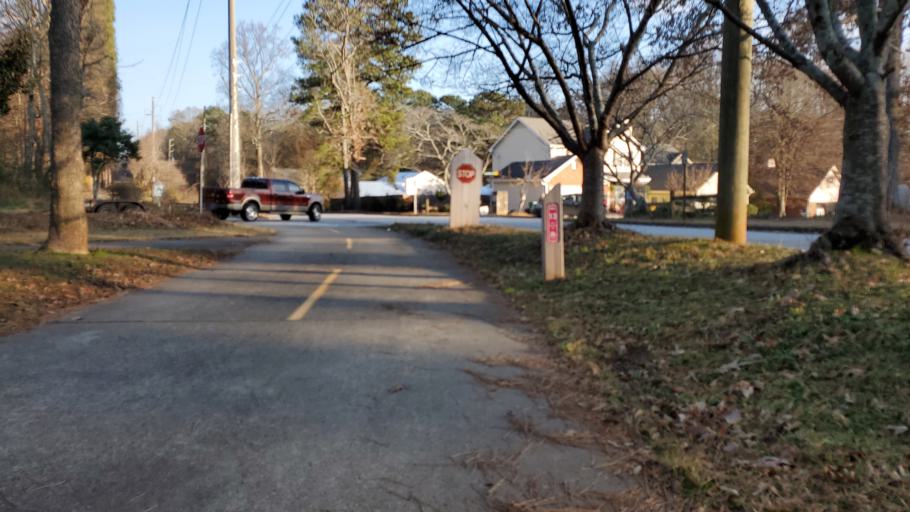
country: US
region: Georgia
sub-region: DeKalb County
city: Clarkston
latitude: 33.8184
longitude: -84.2273
